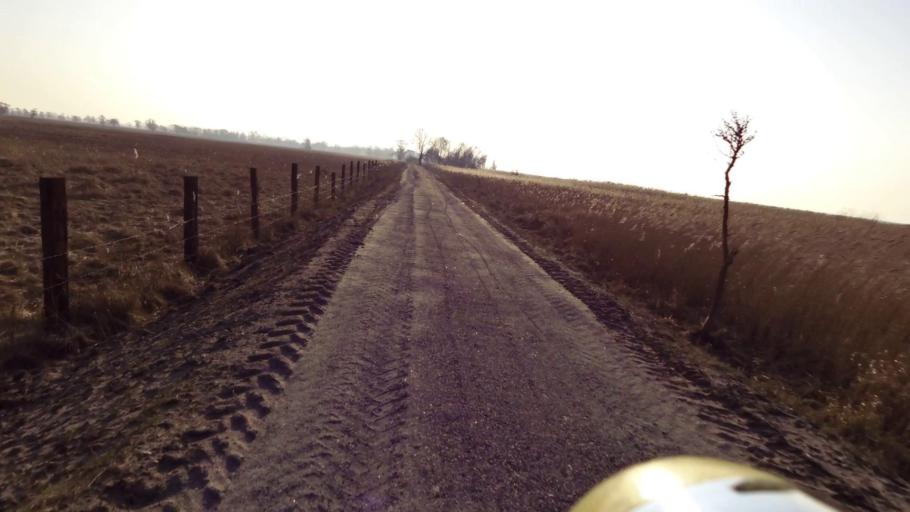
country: PL
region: West Pomeranian Voivodeship
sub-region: Powiat goleniowski
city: Stepnica
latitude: 53.7409
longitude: 14.5563
